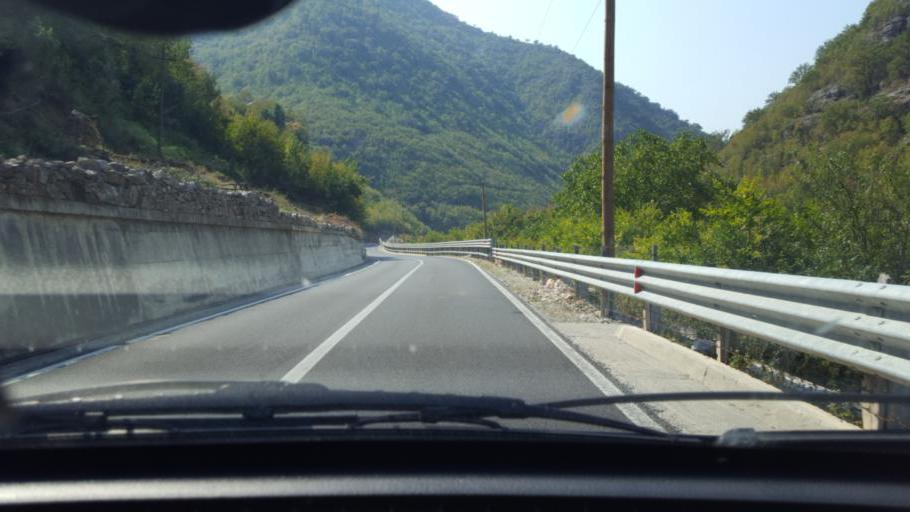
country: AL
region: Shkoder
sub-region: Rrethi i Malesia e Madhe
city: Kastrat
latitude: 42.4279
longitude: 19.5317
